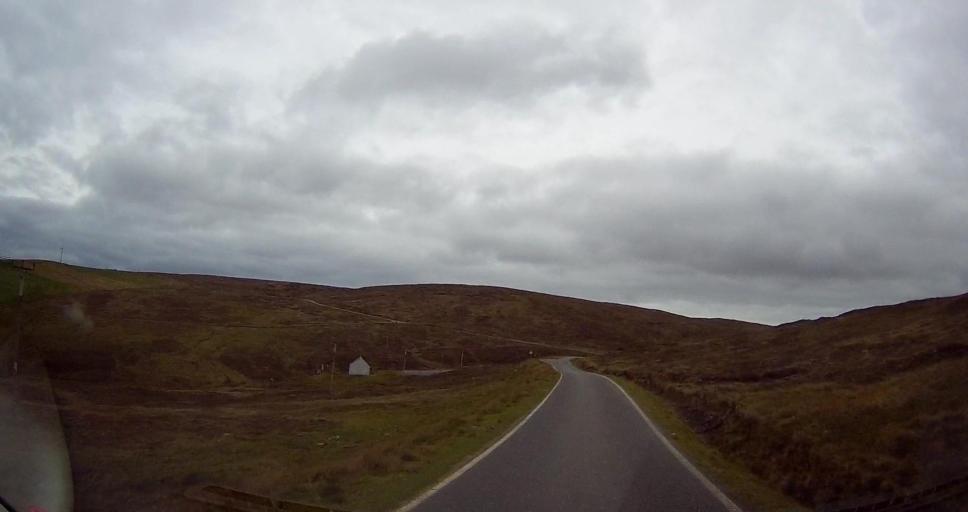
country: GB
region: Scotland
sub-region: Shetland Islands
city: Shetland
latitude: 60.5520
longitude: -1.0582
